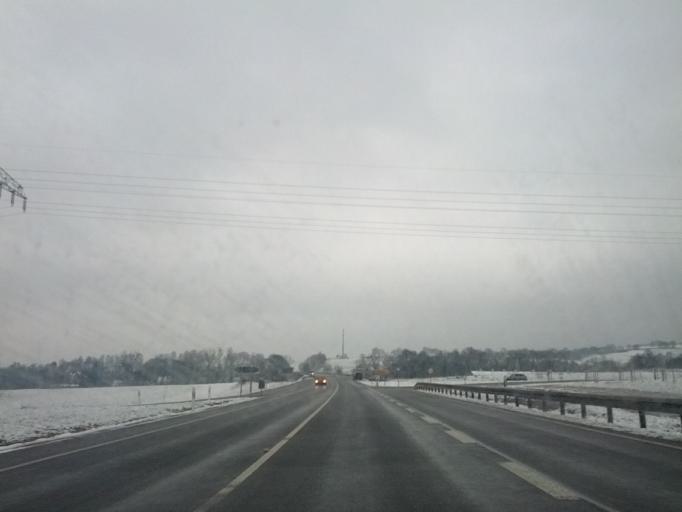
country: DE
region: Thuringia
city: Schwallungen
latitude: 50.7104
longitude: 10.3656
